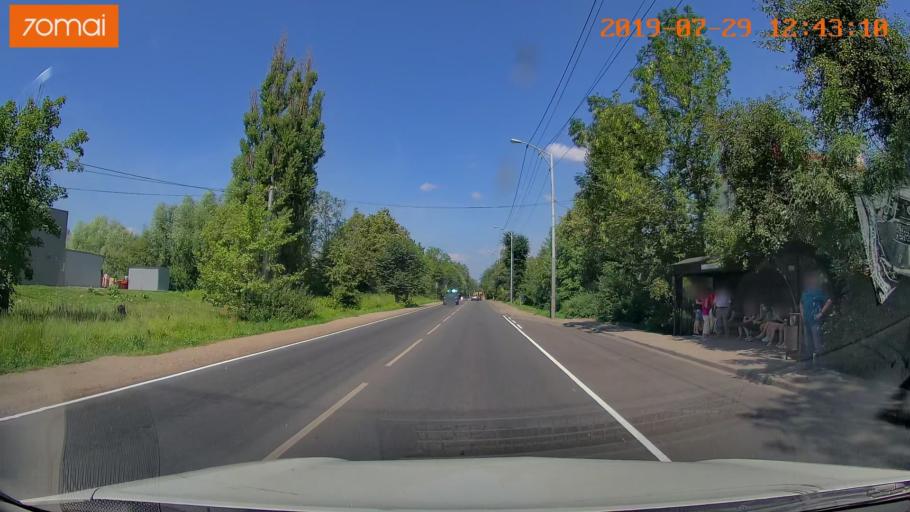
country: RU
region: Kaliningrad
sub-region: Gorod Kaliningrad
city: Kaliningrad
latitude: 54.6742
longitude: 20.5426
